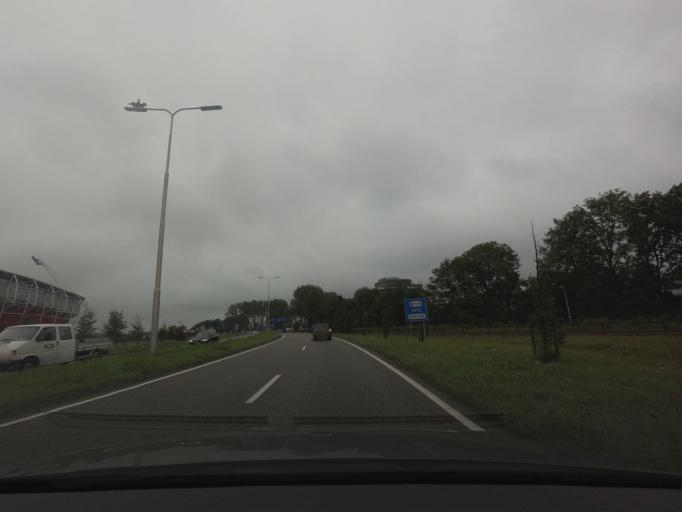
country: NL
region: North Holland
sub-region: Gemeente Alkmaar
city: Alkmaar
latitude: 52.6136
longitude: 4.7444
